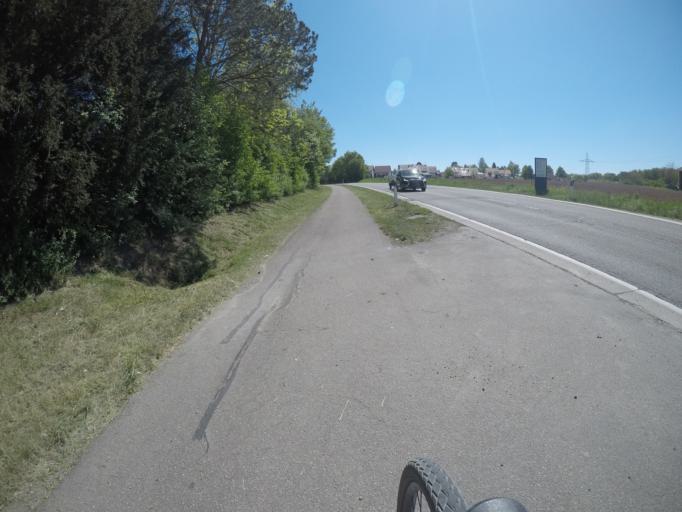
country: DE
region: Baden-Wuerttemberg
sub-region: Regierungsbezirk Stuttgart
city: Waiblingen
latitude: 48.8582
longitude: 9.2920
